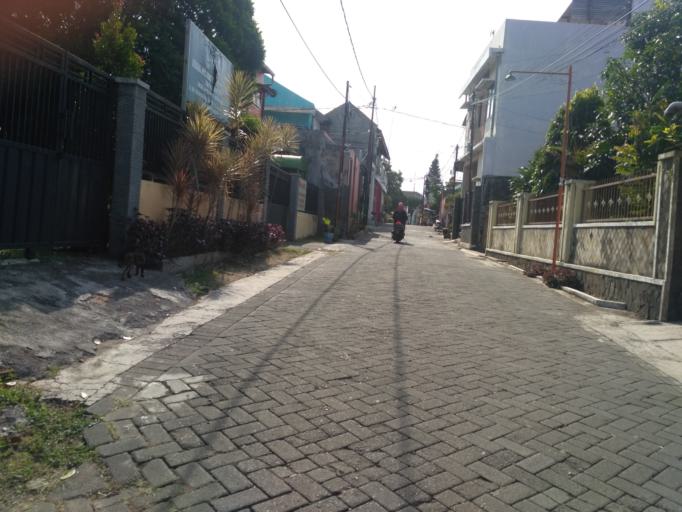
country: ID
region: East Java
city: Malang
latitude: -7.9391
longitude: 112.6103
